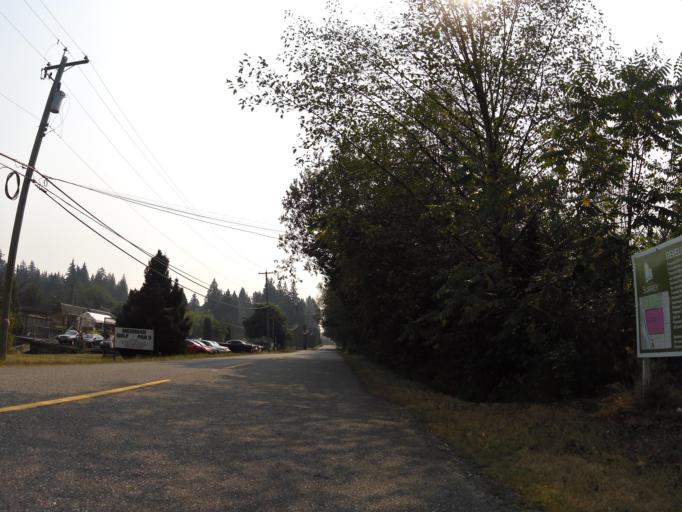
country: US
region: Washington
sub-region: Whatcom County
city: Blaine
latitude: 49.0223
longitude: -122.7572
